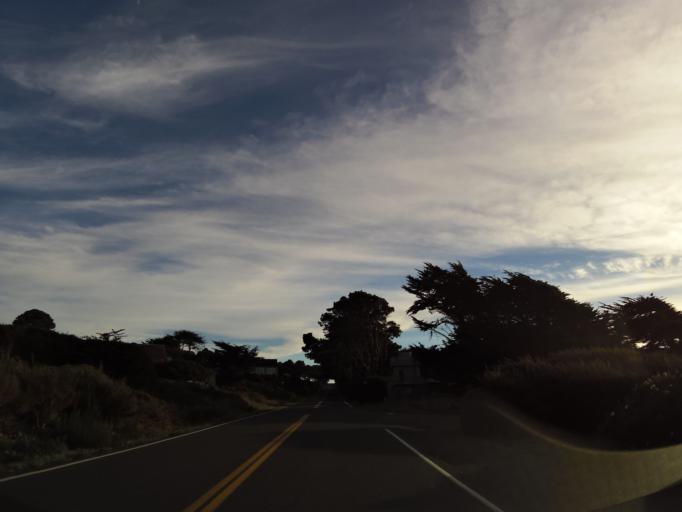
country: US
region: California
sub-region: Mendocino County
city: Fort Bragg
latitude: 39.3133
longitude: -123.8005
